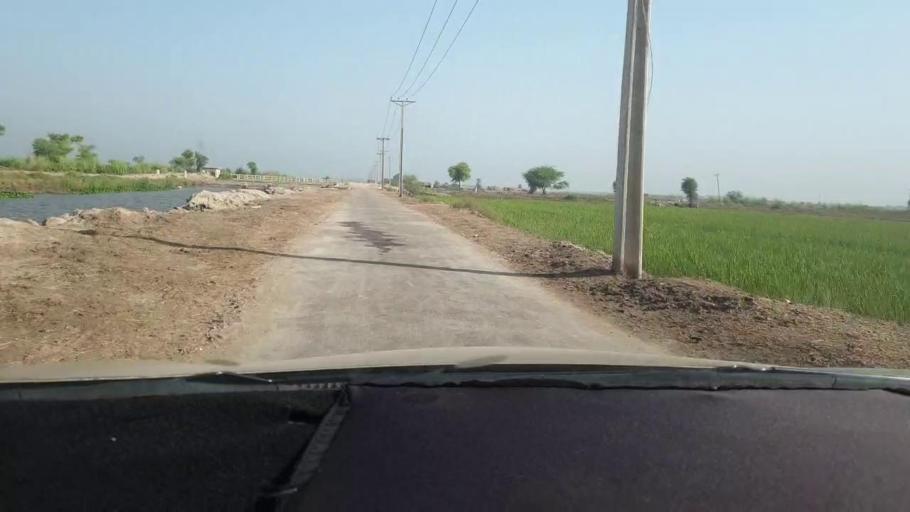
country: PK
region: Sindh
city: Miro Khan
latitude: 27.7625
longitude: 68.1336
